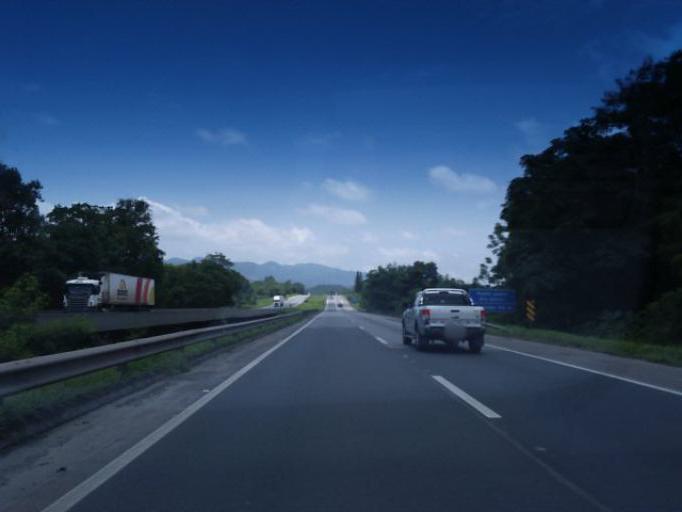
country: BR
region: Sao Paulo
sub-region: Miracatu
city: Miracatu
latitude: -24.2438
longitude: -47.3658
